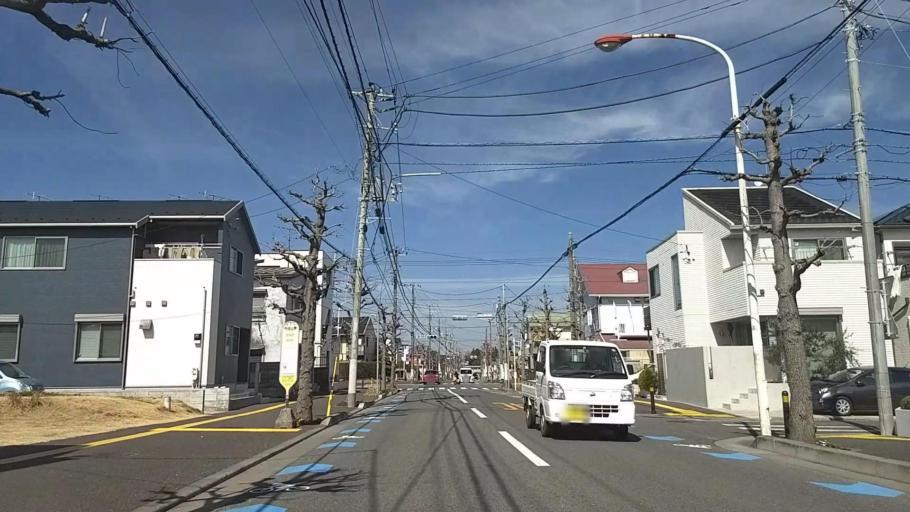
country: JP
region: Kanagawa
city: Fujisawa
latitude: 35.3983
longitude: 139.4729
